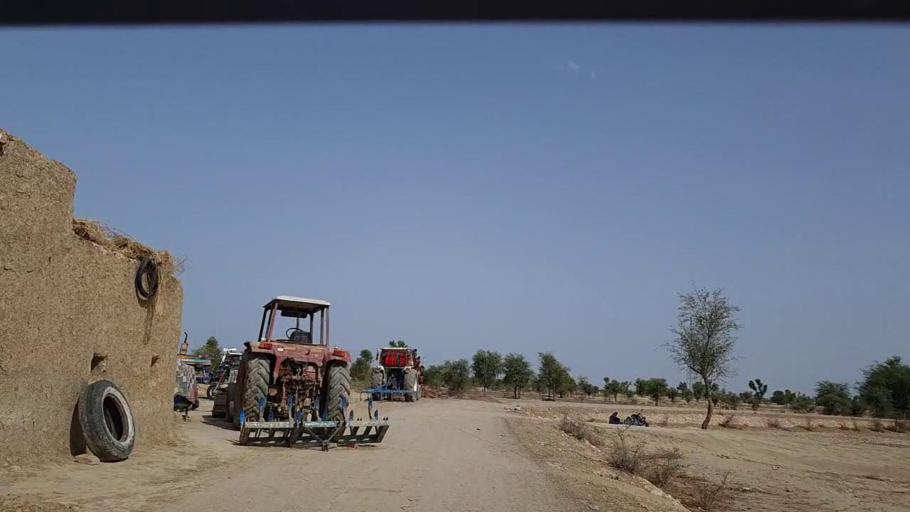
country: PK
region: Sindh
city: Johi
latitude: 26.6405
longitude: 67.5031
